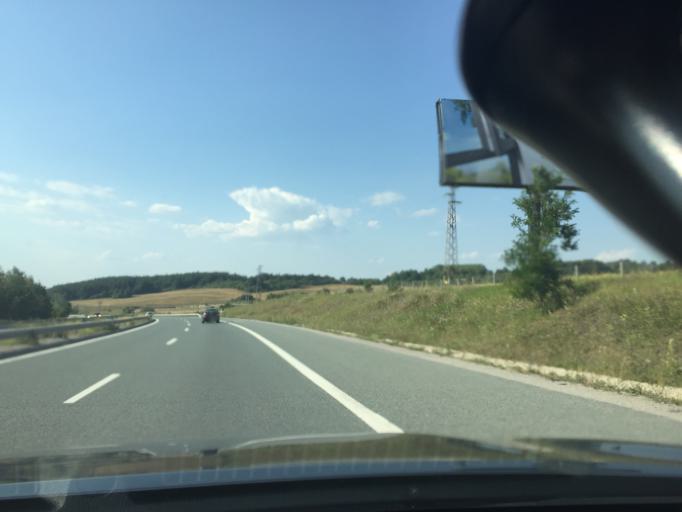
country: BG
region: Pernik
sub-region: Obshtina Pernik
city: Pernik
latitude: 42.5495
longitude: 23.1256
